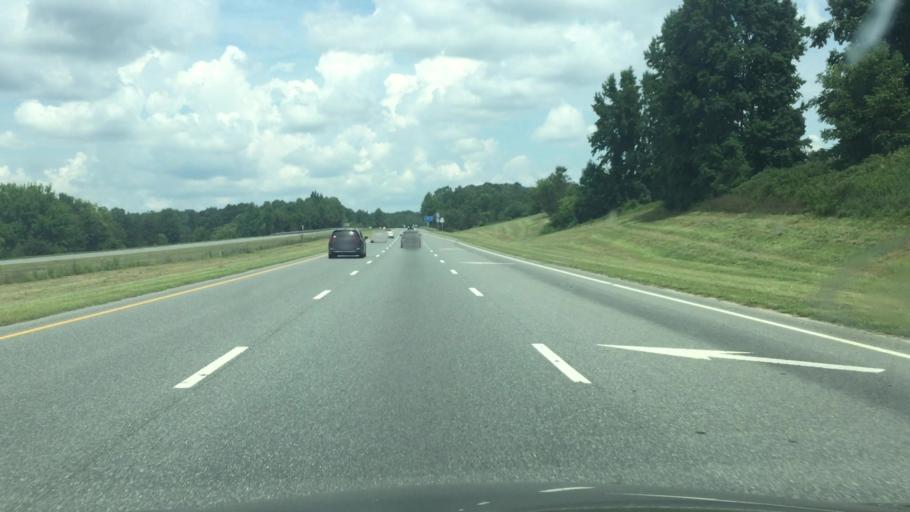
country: US
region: North Carolina
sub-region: Montgomery County
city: Biscoe
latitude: 35.4952
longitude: -79.7802
